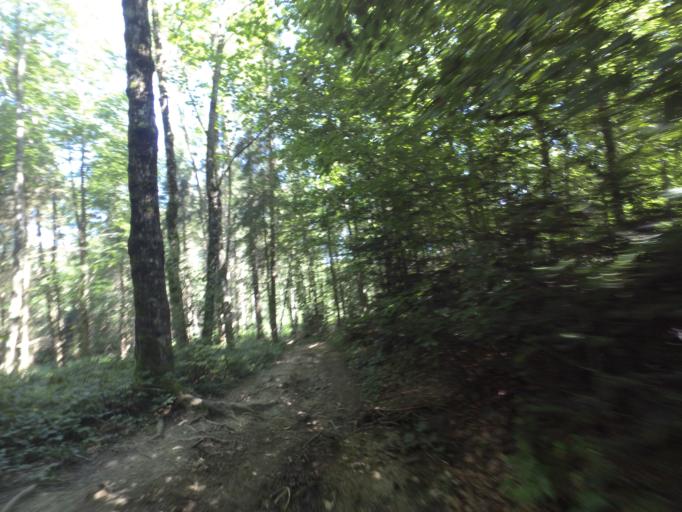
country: AT
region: Salzburg
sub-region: Politischer Bezirk Salzburg-Umgebung
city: Mattsee
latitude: 47.9613
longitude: 13.1143
